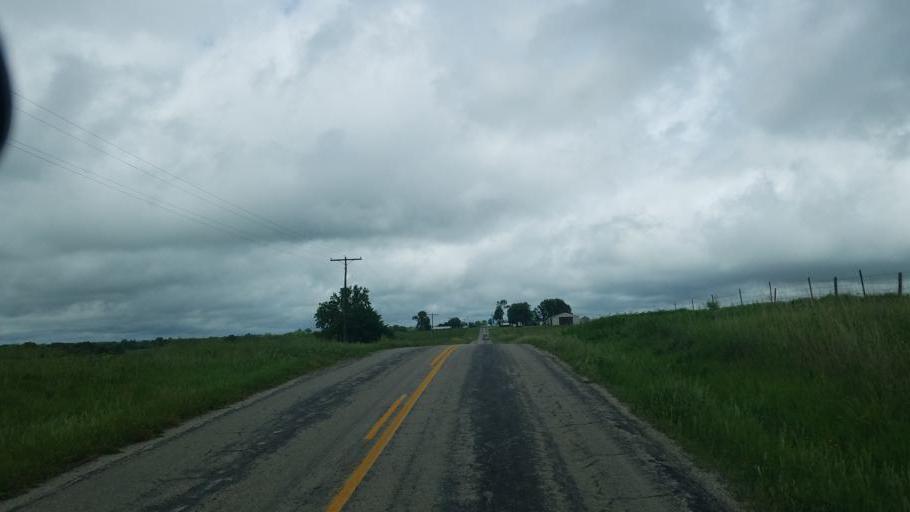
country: US
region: Missouri
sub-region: Mercer County
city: Princeton
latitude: 40.3614
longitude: -93.6806
